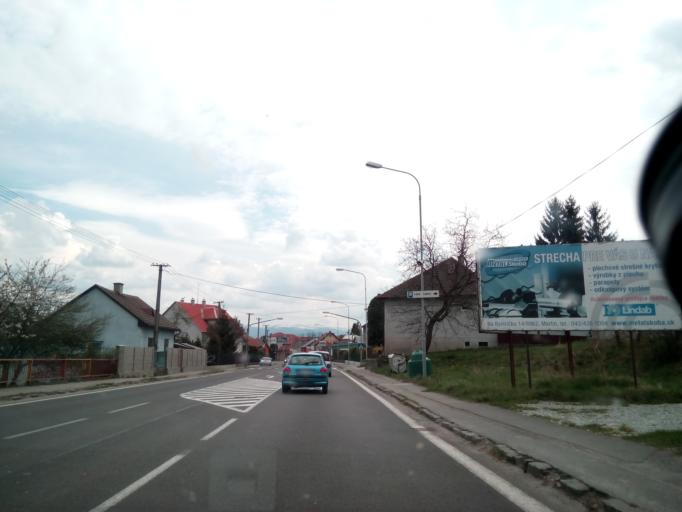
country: SK
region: Zilinsky
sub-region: Okres Zilina
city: Vrutky
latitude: 49.1180
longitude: 18.9120
